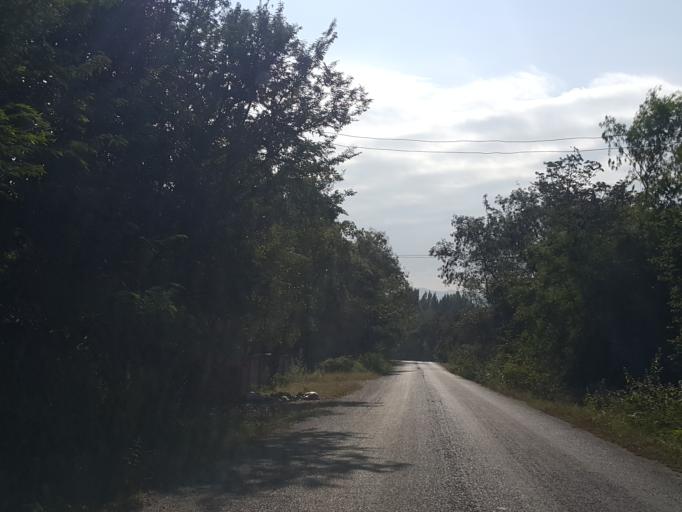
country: TH
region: Lampang
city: Mae Mo
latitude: 18.2953
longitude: 99.6700
